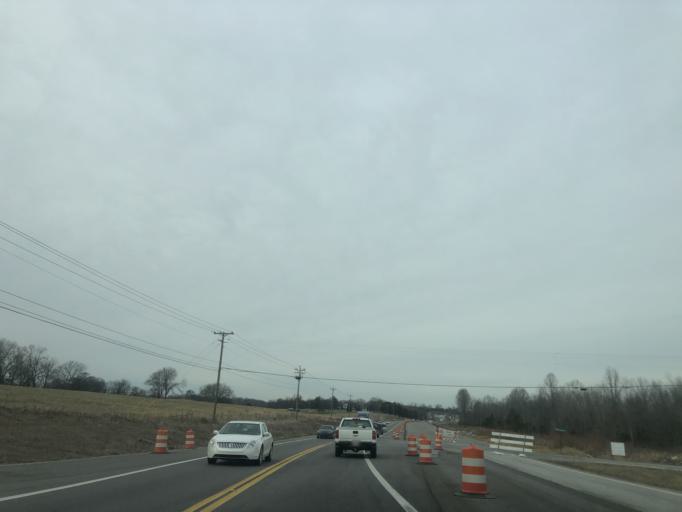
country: US
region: Tennessee
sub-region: Wilson County
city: Mount Juliet
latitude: 36.2789
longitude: -86.4429
